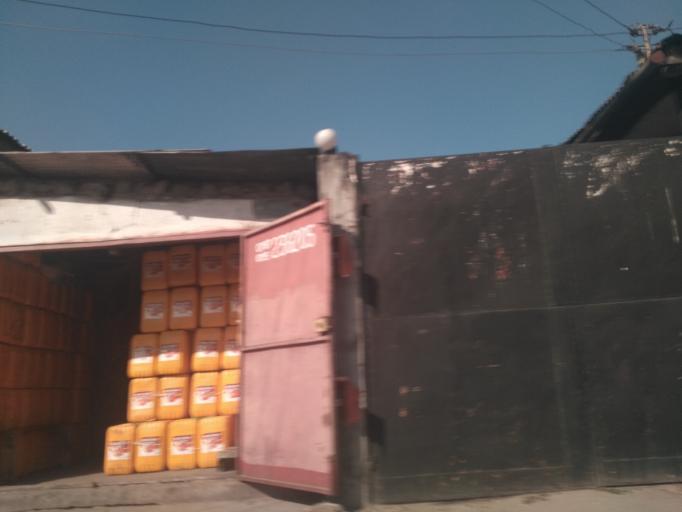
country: TZ
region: Dar es Salaam
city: Dar es Salaam
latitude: -6.8700
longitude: 39.2644
